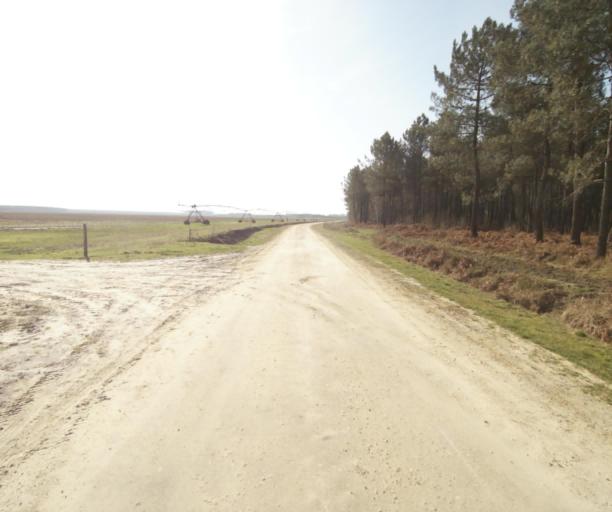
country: FR
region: Aquitaine
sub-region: Departement de la Gironde
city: Grignols
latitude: 44.2122
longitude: -0.1437
